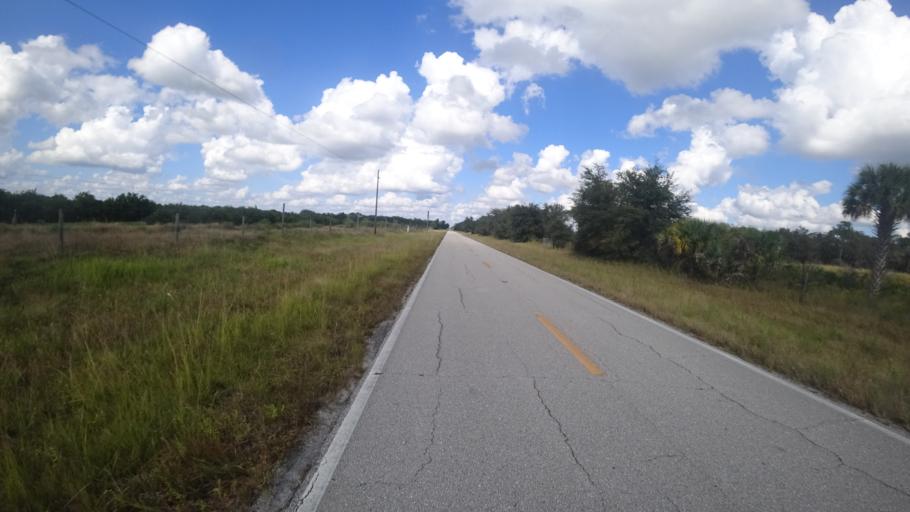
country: US
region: Florida
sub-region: Sarasota County
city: North Port
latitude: 27.2301
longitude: -82.1220
